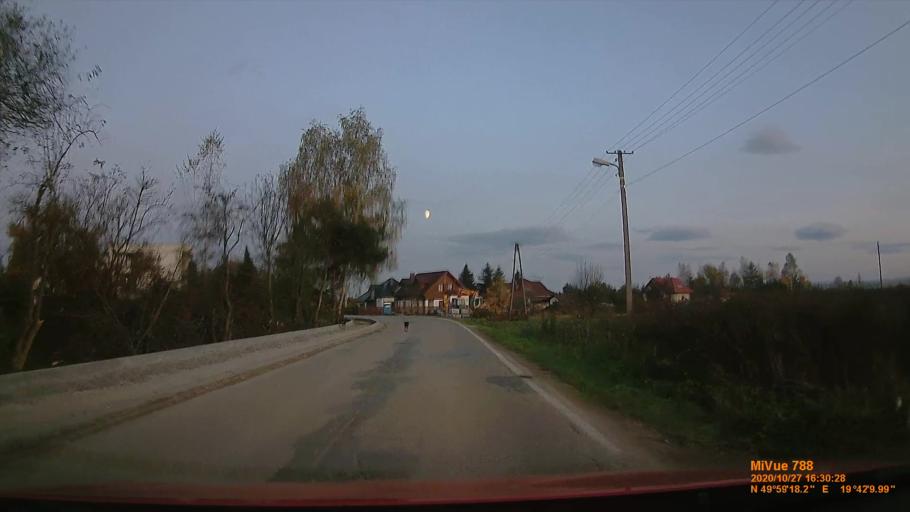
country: PL
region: Lesser Poland Voivodeship
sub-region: Powiat krakowski
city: Czernichow
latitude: 49.9884
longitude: 19.7030
